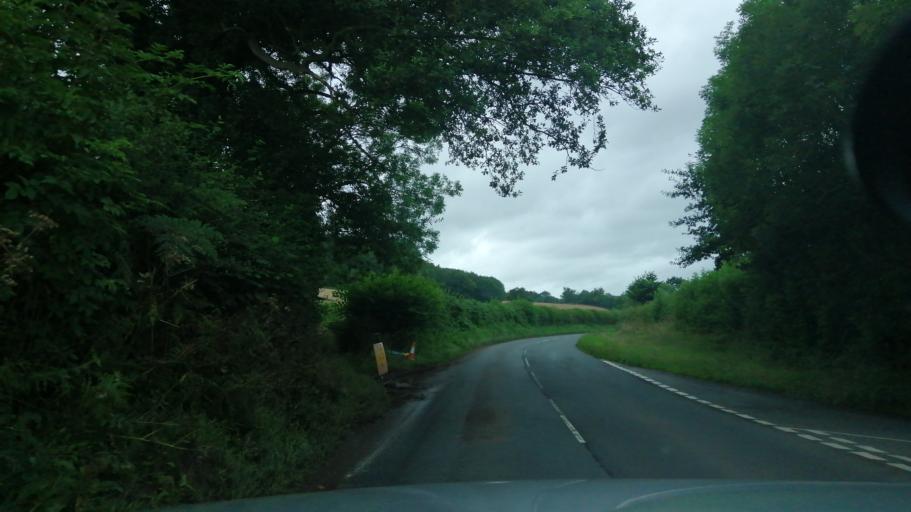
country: GB
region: England
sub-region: Herefordshire
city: Madley
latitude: 52.0198
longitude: -2.8655
